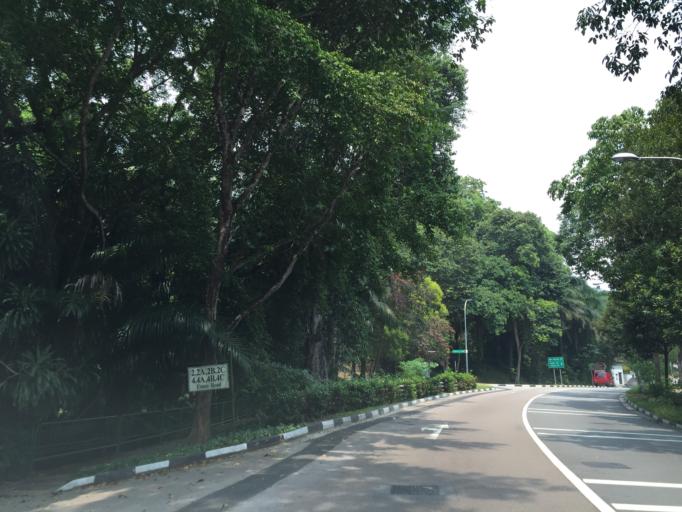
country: SG
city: Singapore
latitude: 1.3166
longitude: 103.8190
